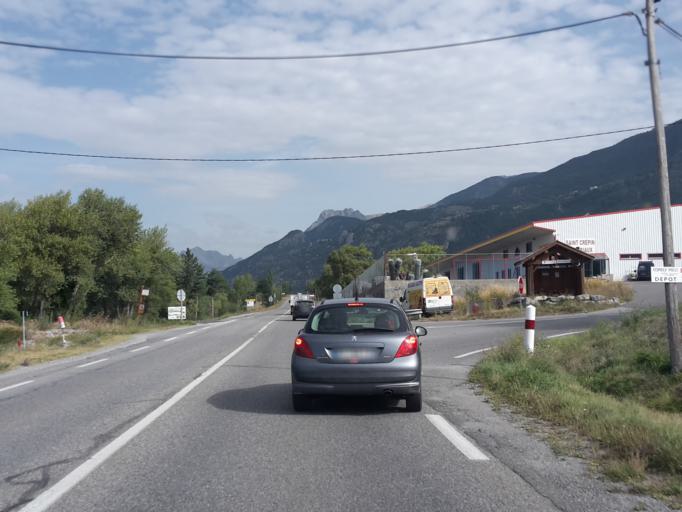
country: FR
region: Provence-Alpes-Cote d'Azur
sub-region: Departement des Hautes-Alpes
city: Guillestre
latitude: 44.6835
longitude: 6.6147
